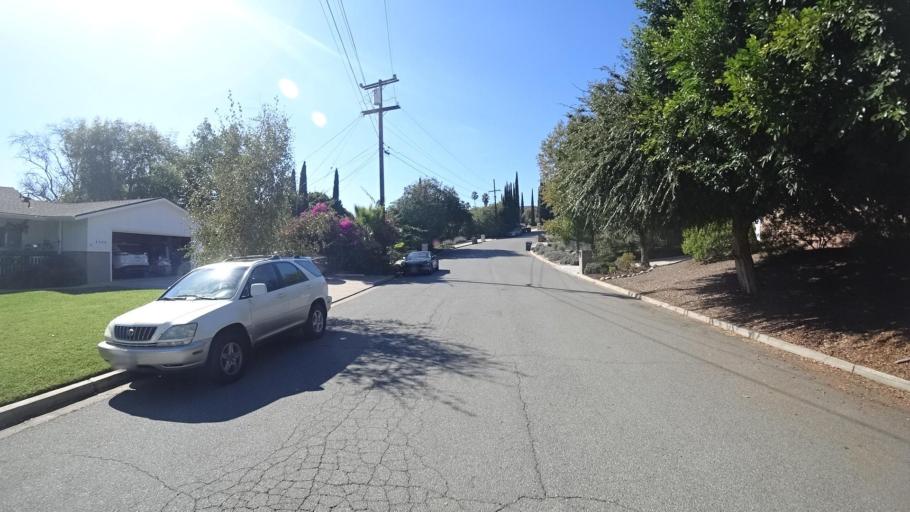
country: US
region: California
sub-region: San Diego County
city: Casa de Oro-Mount Helix
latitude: 32.7600
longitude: -116.9764
